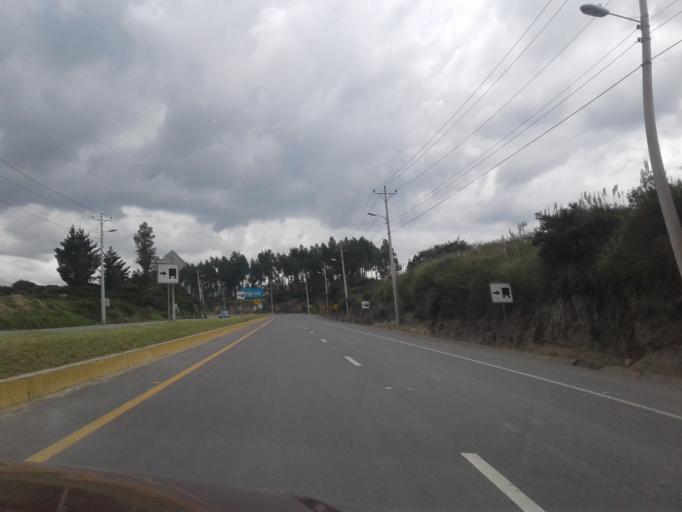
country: EC
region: Pichincha
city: Sangolqui
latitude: -0.3061
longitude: -78.3629
